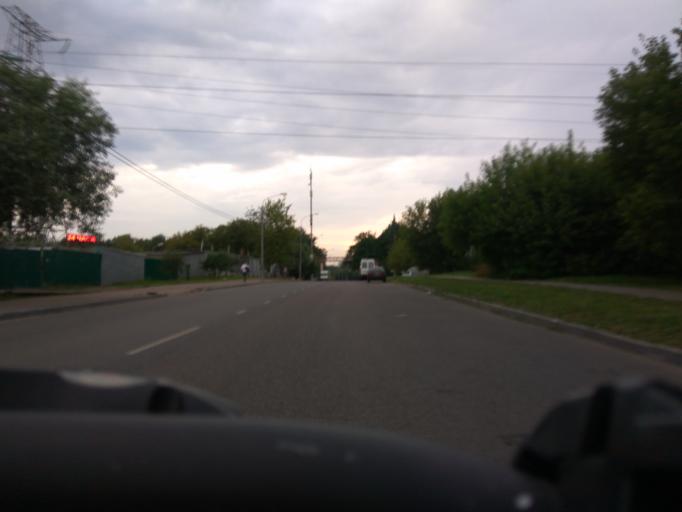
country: RU
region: Moscow
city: Tsaritsyno
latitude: 55.6245
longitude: 37.6455
